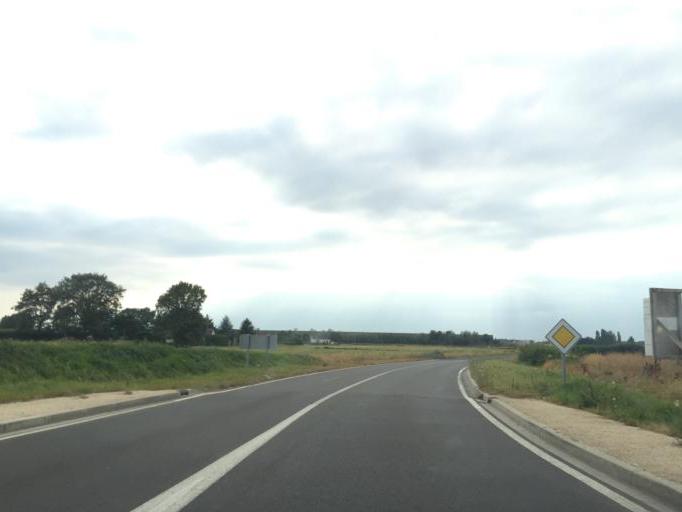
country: FR
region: Auvergne
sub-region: Departement de l'Allier
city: Lusigny
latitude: 46.5362
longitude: 3.4421
